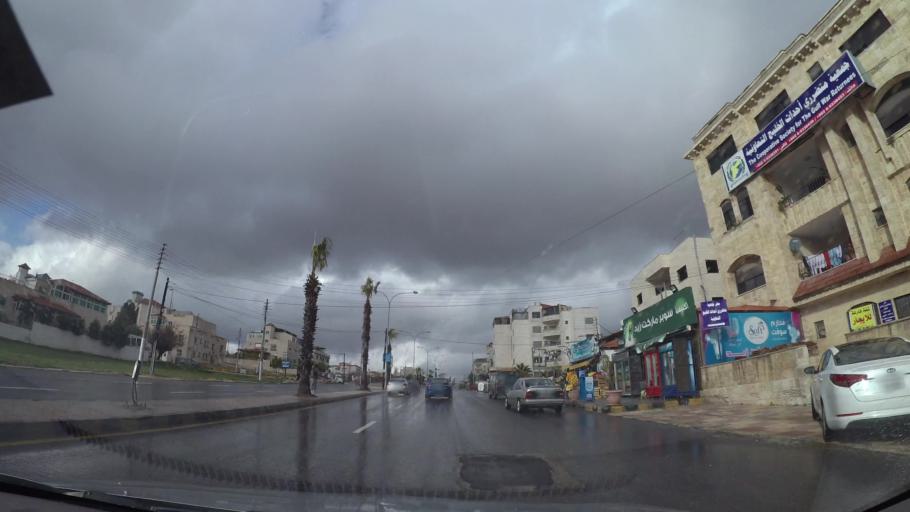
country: JO
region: Amman
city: Al Jubayhah
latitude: 32.0339
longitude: 35.8637
